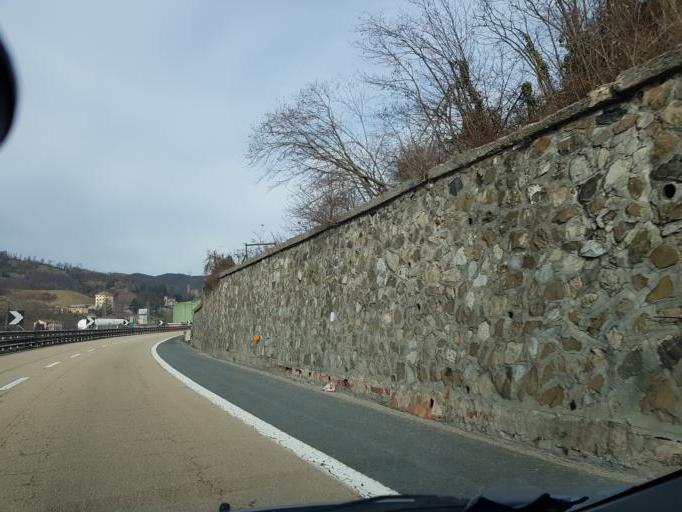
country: IT
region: Liguria
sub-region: Provincia di Genova
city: Busalla
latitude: 44.5777
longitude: 8.9440
